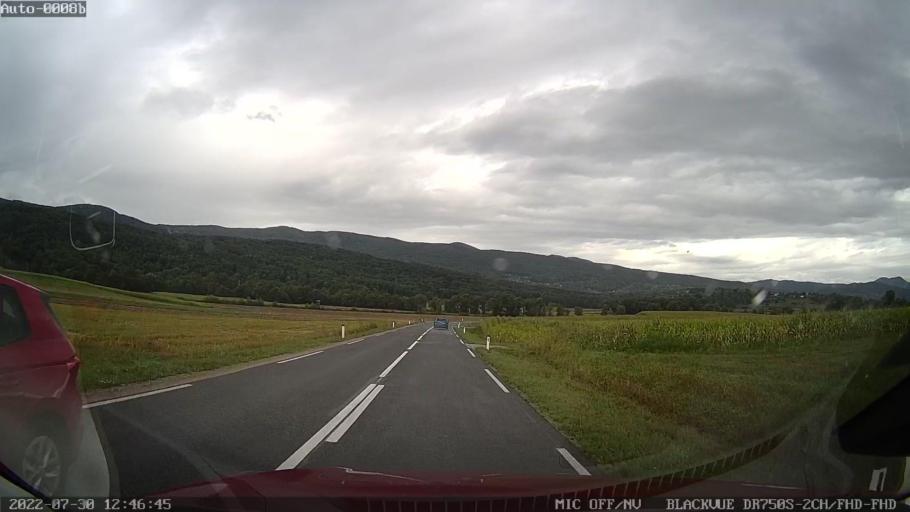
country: SI
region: Crnomelj
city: Crnomelj
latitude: 45.5211
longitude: 15.1715
